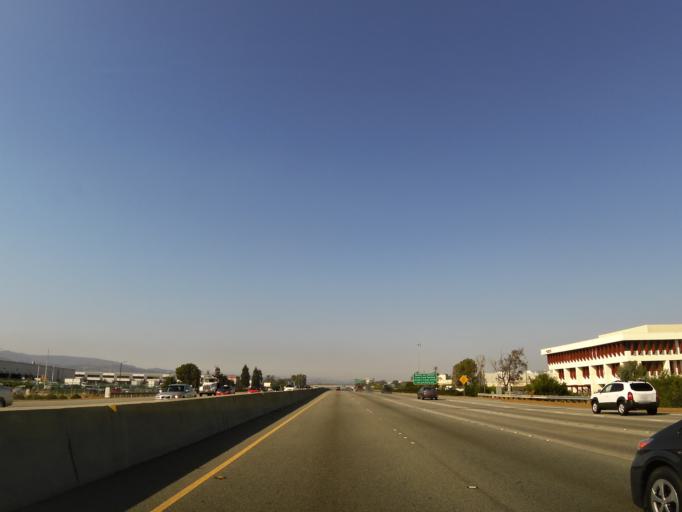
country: US
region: California
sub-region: San Mateo County
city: Millbrae
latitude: 37.5977
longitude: -122.3729
